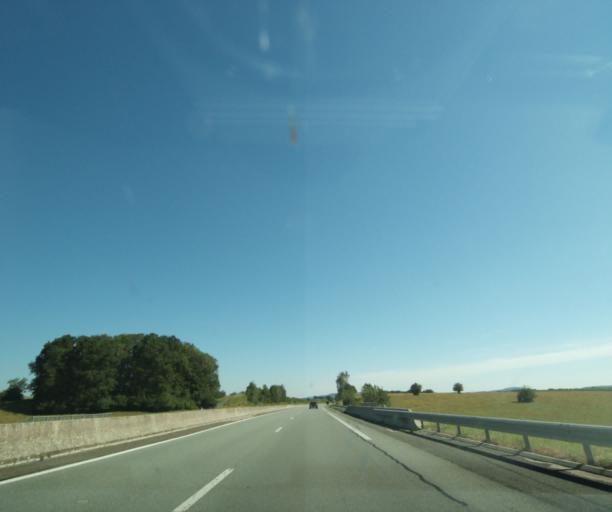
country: FR
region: Champagne-Ardenne
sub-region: Departement de la Haute-Marne
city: Avrecourt
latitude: 48.0053
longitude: 5.5172
